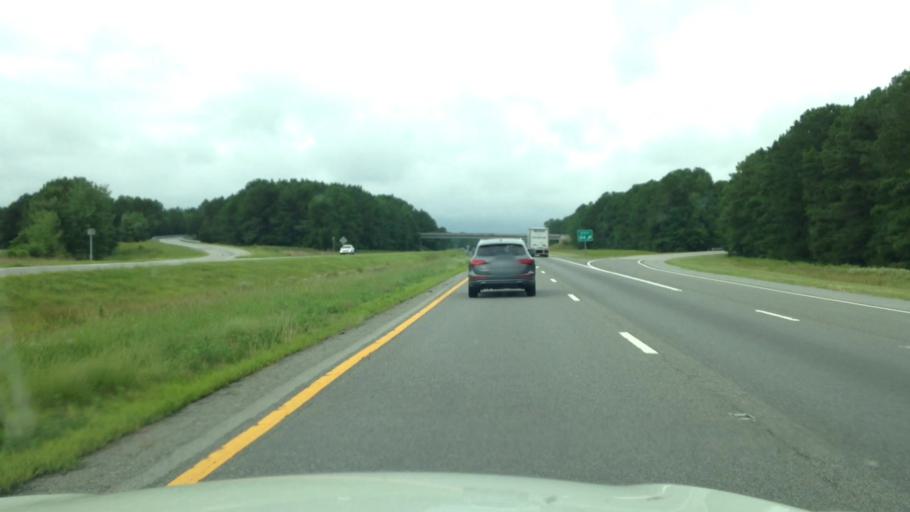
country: US
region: Virginia
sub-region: Sussex County
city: Sussex
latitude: 36.8564
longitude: -77.4206
